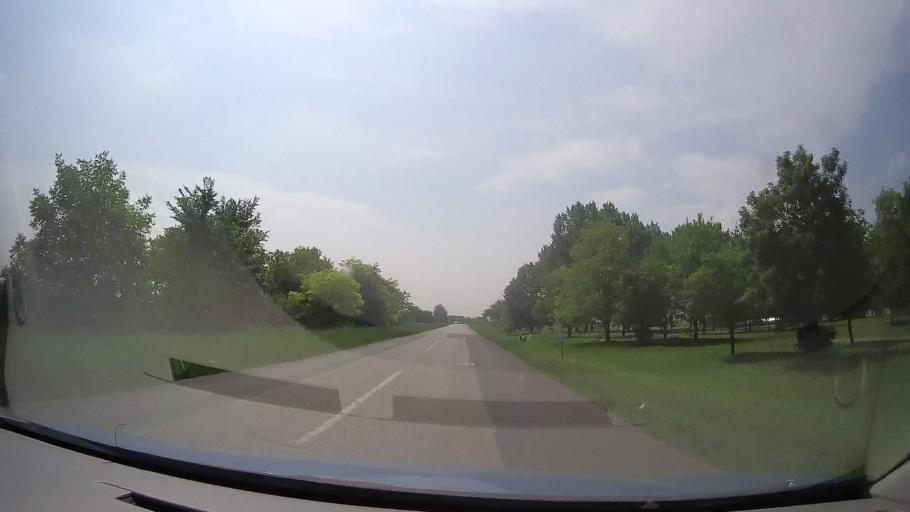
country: RS
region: Autonomna Pokrajina Vojvodina
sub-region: Juznobanatski Okrug
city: Kovacica
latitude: 45.0867
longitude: 20.6370
